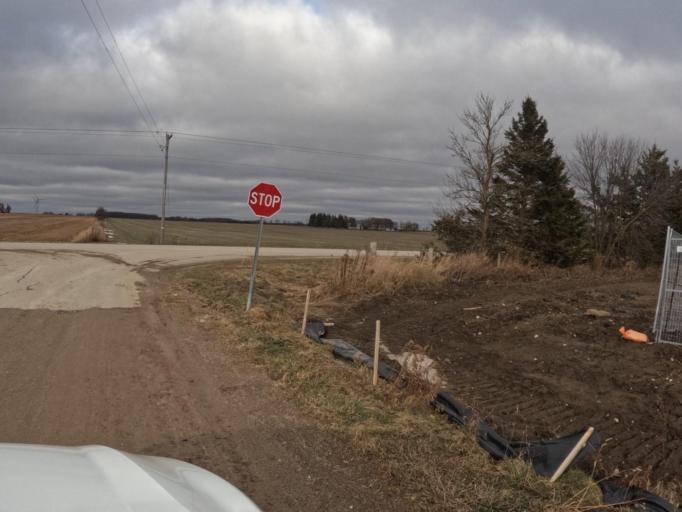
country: CA
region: Ontario
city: Shelburne
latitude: 43.8957
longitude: -80.3301
